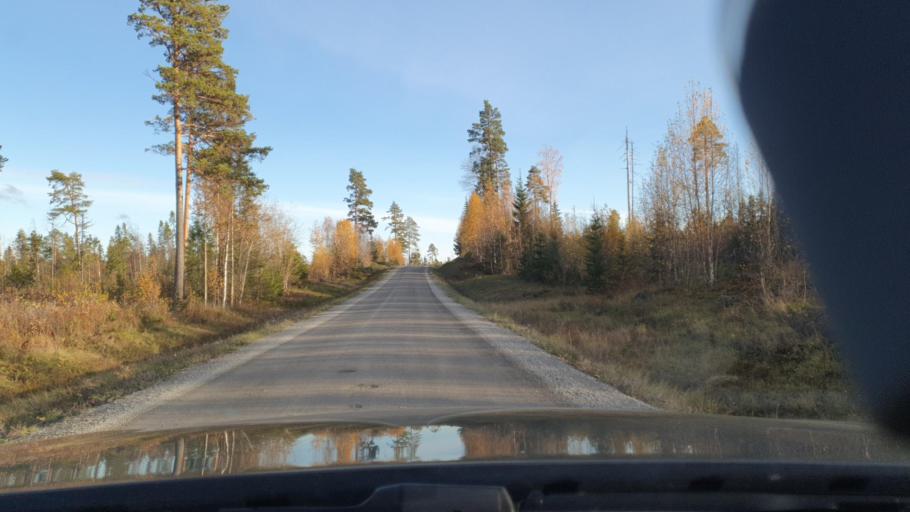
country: SE
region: Jaemtland
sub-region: Stroemsunds Kommun
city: Stroemsund
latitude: 63.5553
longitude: 15.5450
